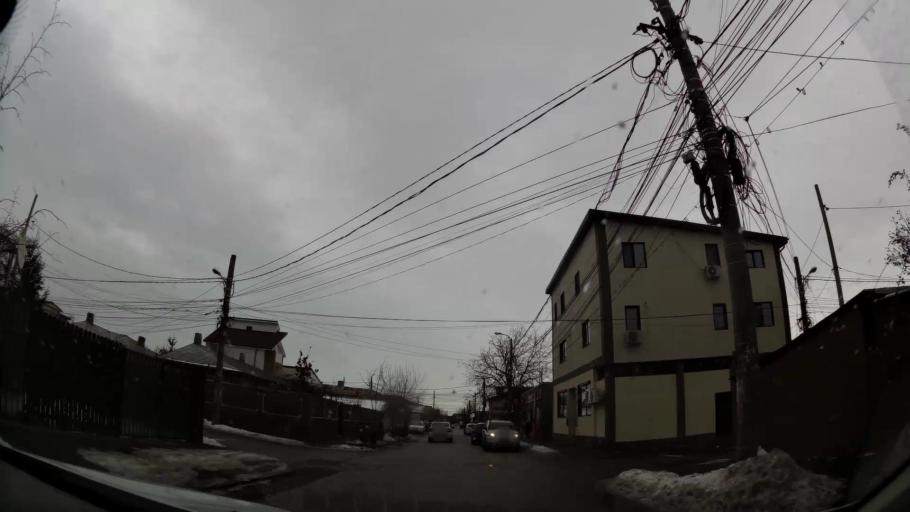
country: RO
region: Ilfov
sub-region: Comuna Pantelimon
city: Pantelimon
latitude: 44.4325
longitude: 26.2028
